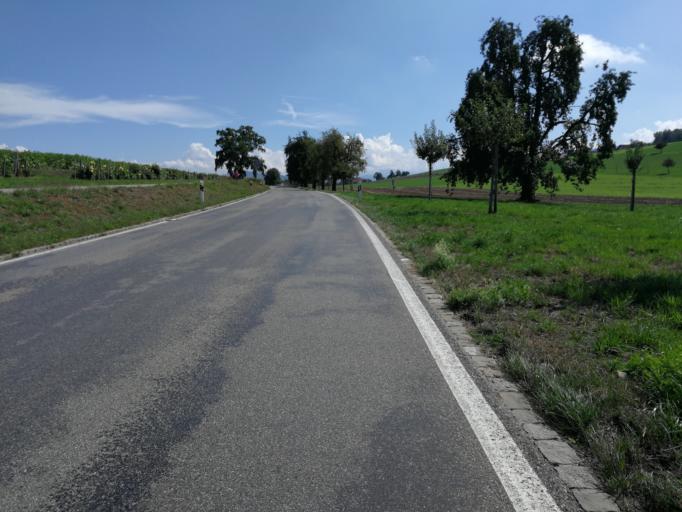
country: CH
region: Zurich
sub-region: Bezirk Horgen
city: Waedenswil / Hangenmoos
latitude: 47.2253
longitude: 8.6489
